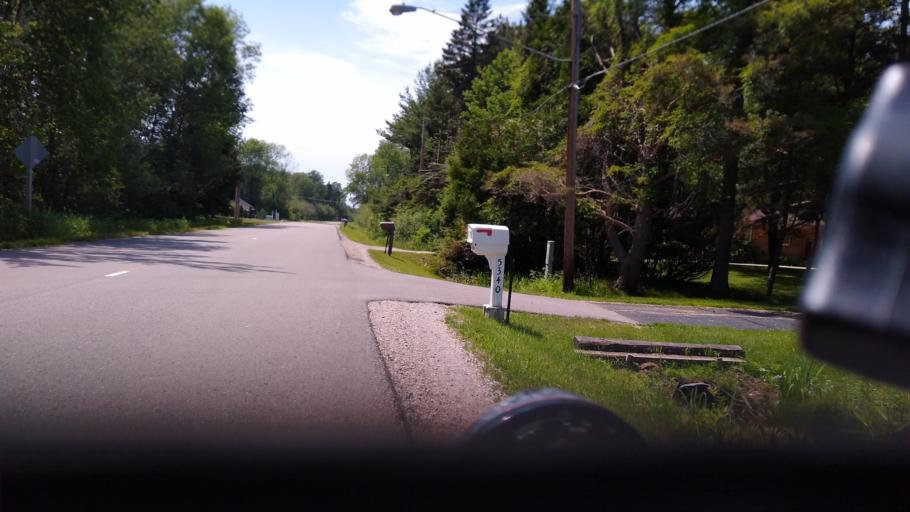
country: US
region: Michigan
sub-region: Delta County
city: Escanaba
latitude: 45.7100
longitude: -87.0988
